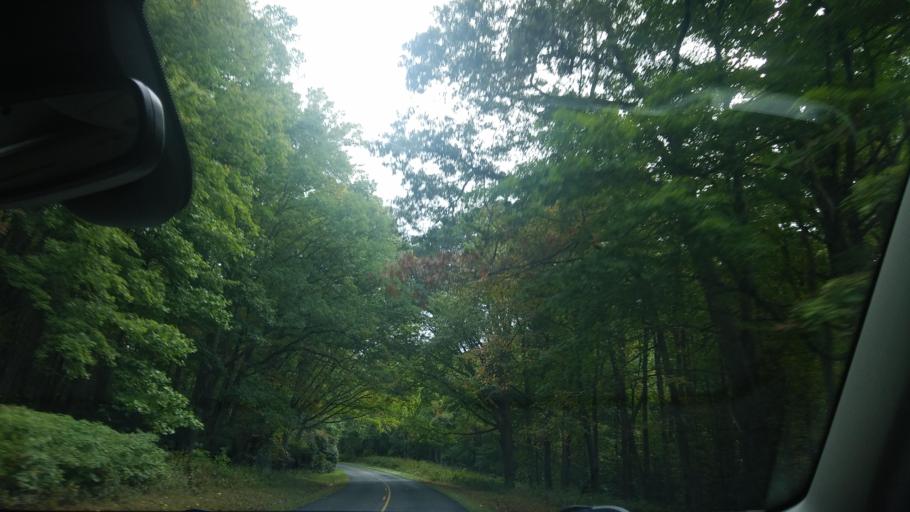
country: US
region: North Carolina
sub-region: Surry County
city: Flat Rock
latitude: 36.6415
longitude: -80.5416
